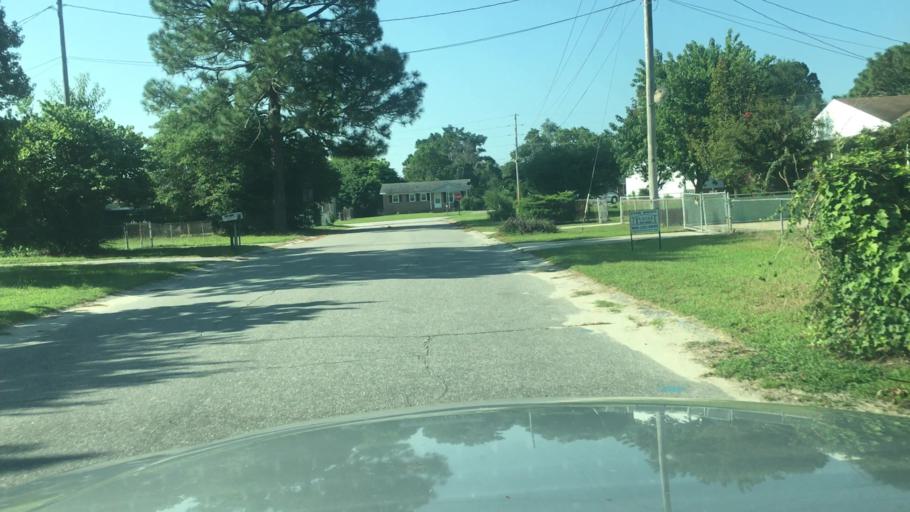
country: US
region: North Carolina
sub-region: Cumberland County
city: Spring Lake
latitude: 35.1525
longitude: -78.9196
